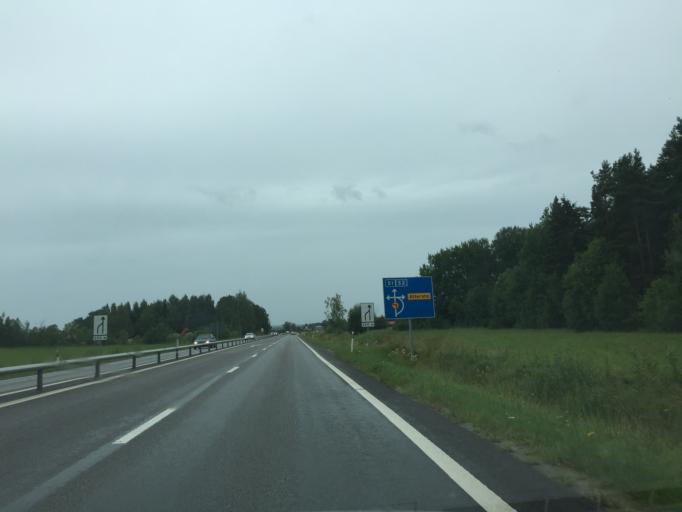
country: SE
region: OErebro
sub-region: Orebro Kommun
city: Orebro
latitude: 59.2028
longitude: 15.2414
